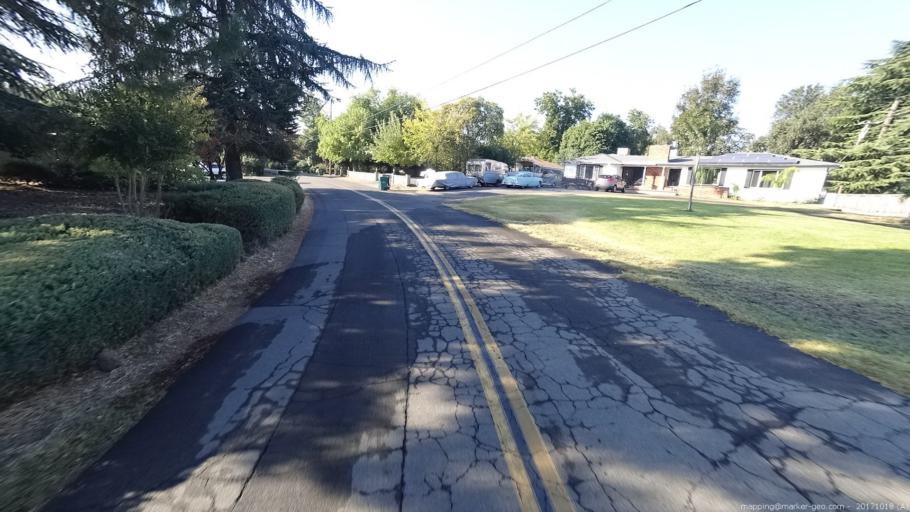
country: US
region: California
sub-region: Shasta County
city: Redding
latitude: 40.5611
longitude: -122.3726
